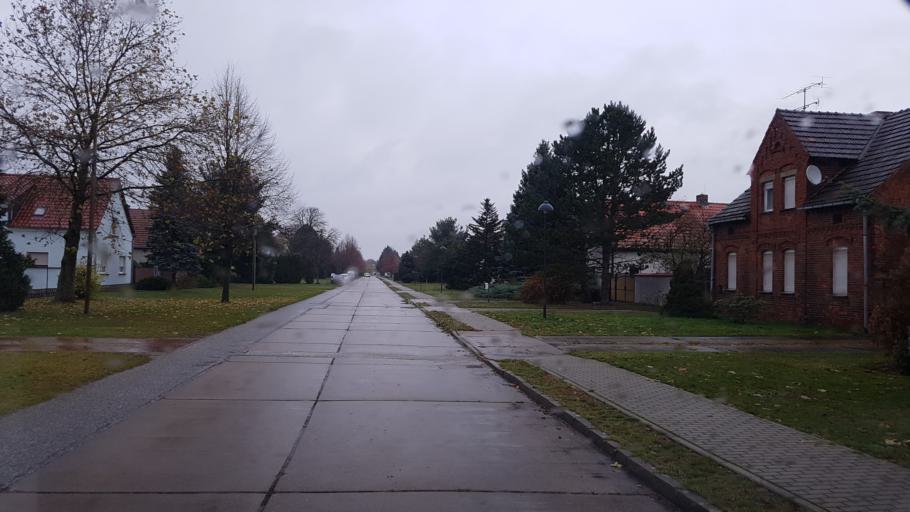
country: DE
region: Brandenburg
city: Herzberg
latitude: 51.6539
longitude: 13.2227
